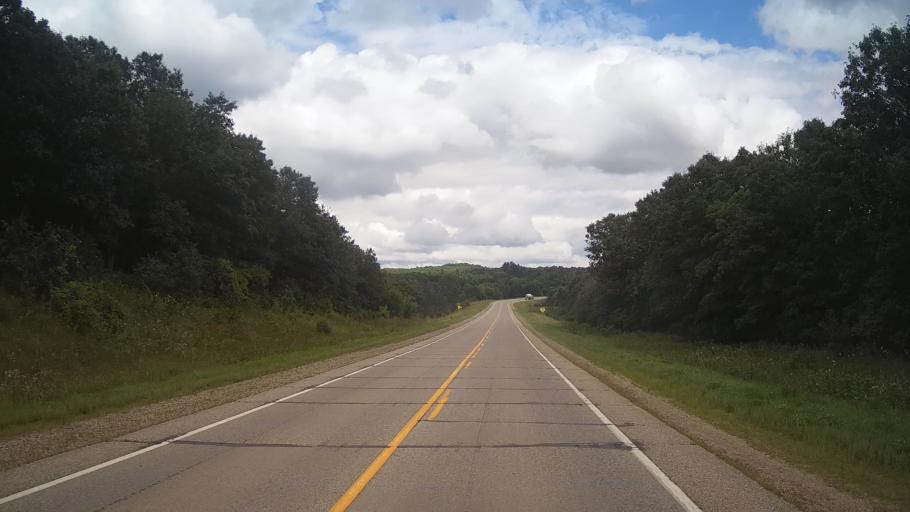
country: US
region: Wisconsin
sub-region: Marquette County
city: Westfield
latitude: 44.0267
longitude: -89.5401
